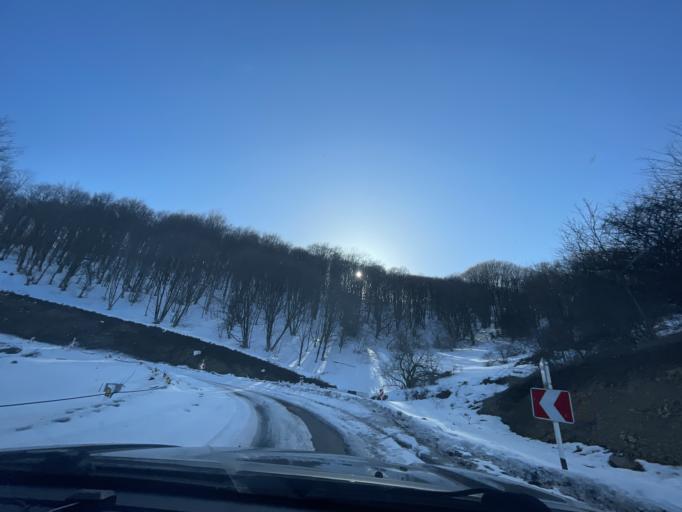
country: GE
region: Kvemo Kartli
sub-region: Tetri Tsqaro
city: Manglisi
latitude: 41.7714
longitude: 44.5062
